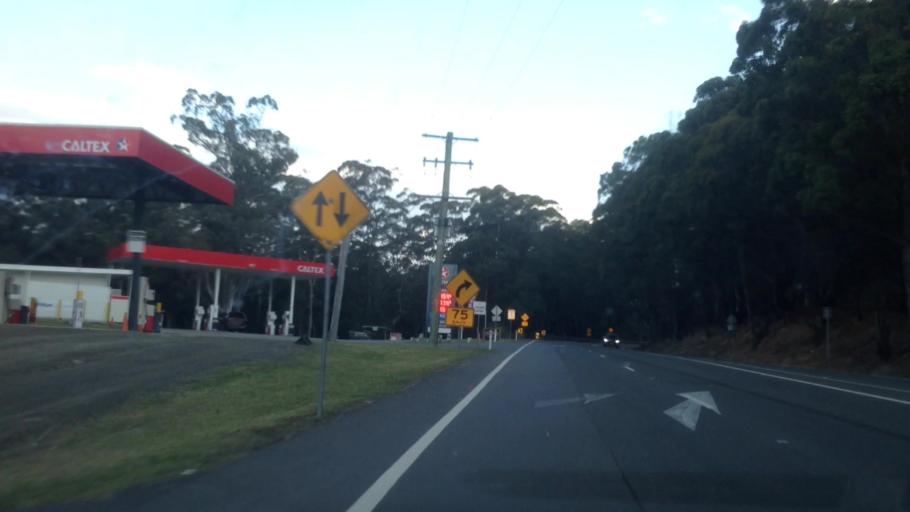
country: AU
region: New South Wales
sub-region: Lake Macquarie Shire
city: Cooranbong
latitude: -32.9640
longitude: 151.4791
